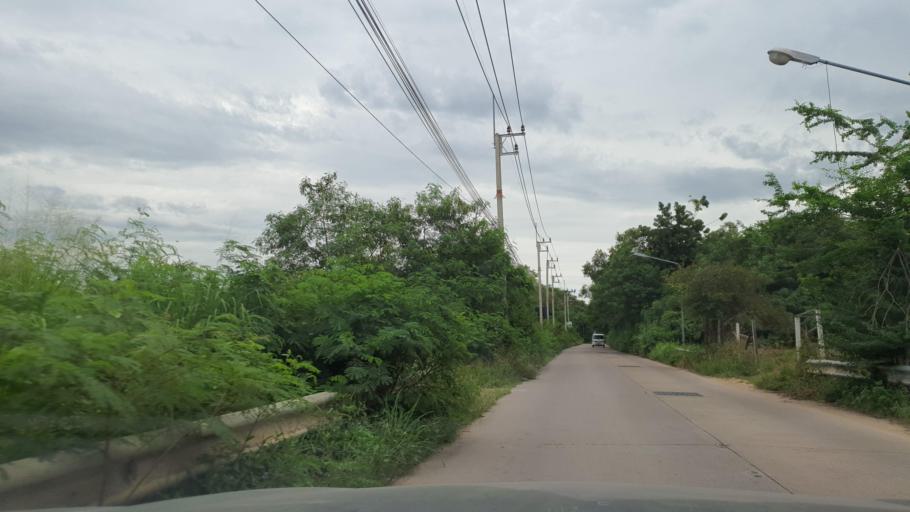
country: TH
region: Chon Buri
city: Phatthaya
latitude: 12.8674
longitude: 100.8980
